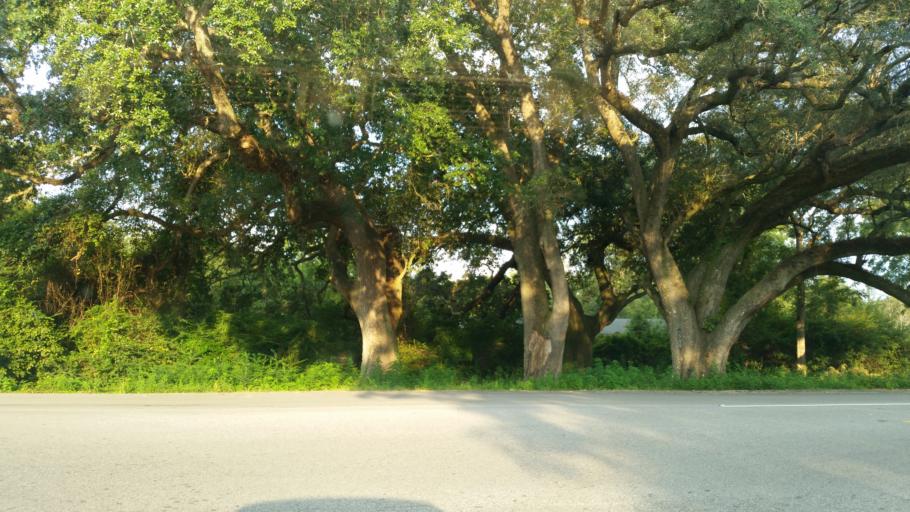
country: US
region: Florida
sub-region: Santa Rosa County
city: Pace
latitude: 30.5997
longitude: -87.1114
